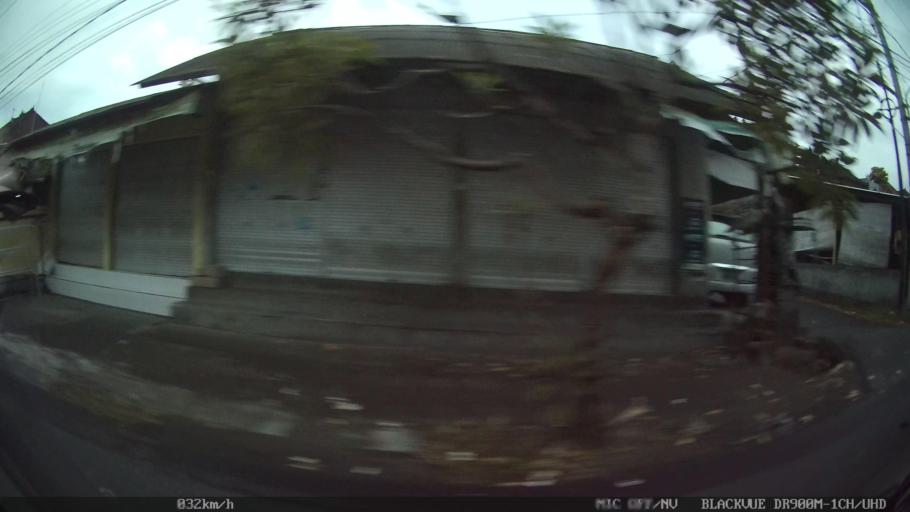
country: ID
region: Bali
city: Banjar Pasekan
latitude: -8.6176
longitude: 115.2703
